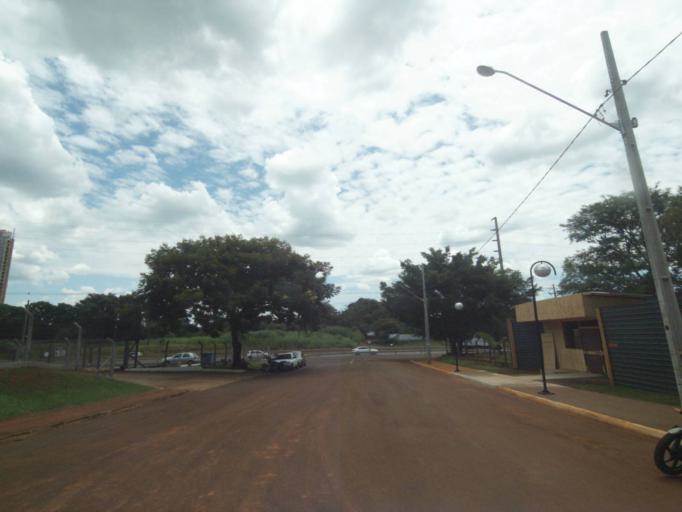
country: BR
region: Parana
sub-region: Londrina
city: Londrina
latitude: -23.3345
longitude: -51.1840
